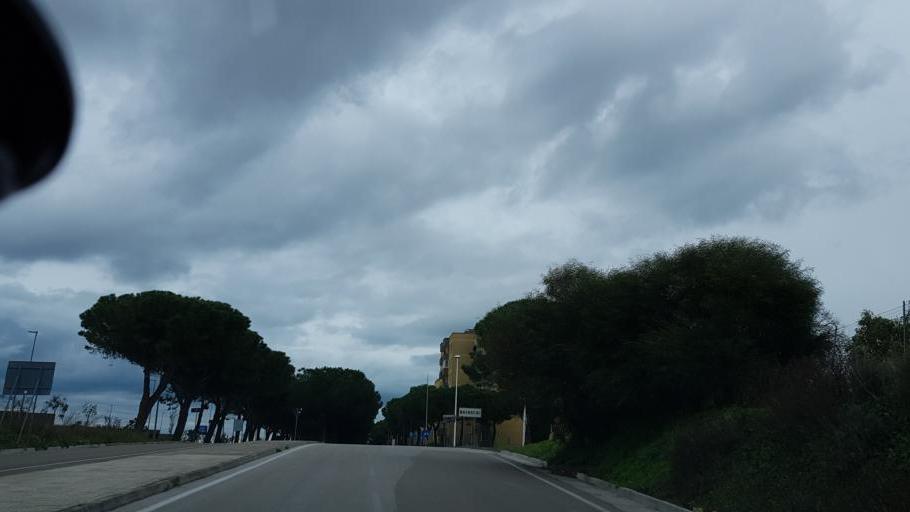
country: IT
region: Apulia
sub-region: Provincia di Brindisi
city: Brindisi
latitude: 40.6215
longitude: 17.9137
